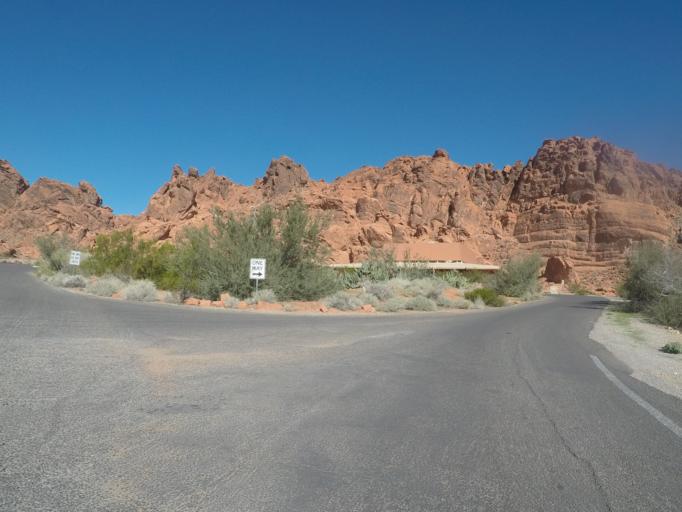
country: US
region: Nevada
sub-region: Clark County
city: Moapa Valley
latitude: 36.4293
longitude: -114.5137
